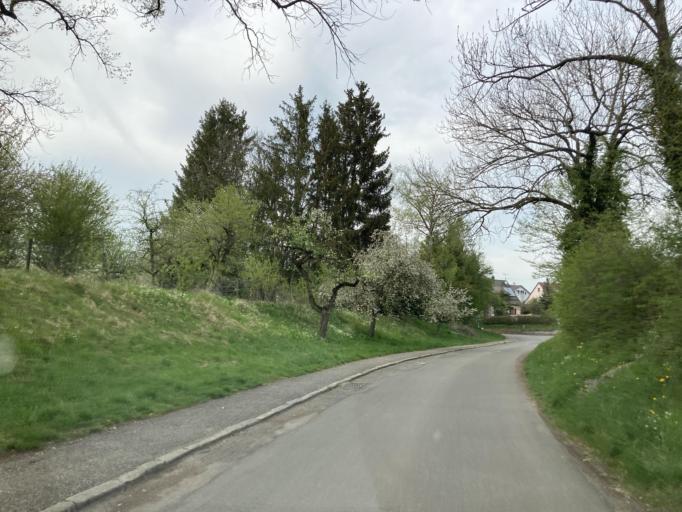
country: DE
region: Baden-Wuerttemberg
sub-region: Tuebingen Region
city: Dusslingen
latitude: 48.4804
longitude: 8.9999
